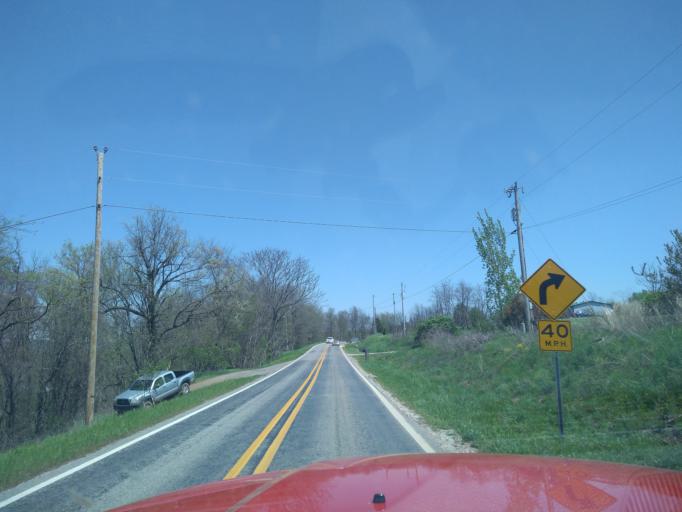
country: US
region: Arkansas
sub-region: Washington County
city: West Fork
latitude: 35.8815
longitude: -94.2429
